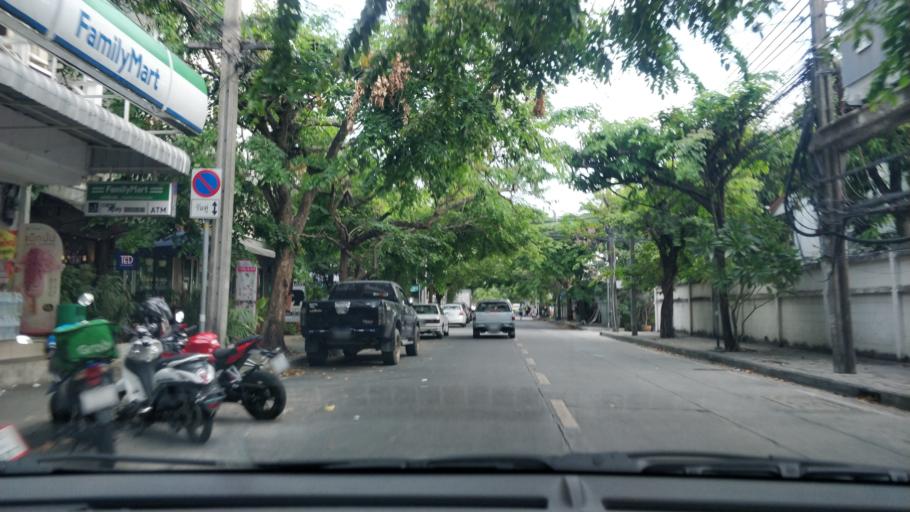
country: TH
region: Bangkok
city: Bang Kapi
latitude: 13.7463
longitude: 100.6315
